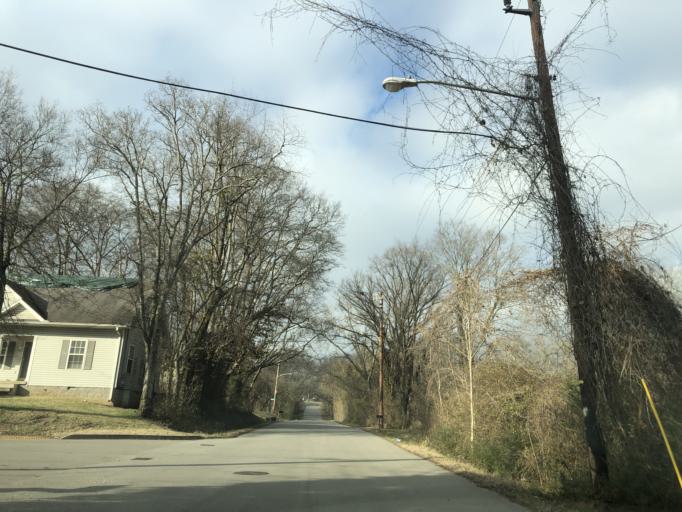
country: US
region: Tennessee
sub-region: Davidson County
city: Nashville
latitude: 36.2044
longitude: -86.7837
